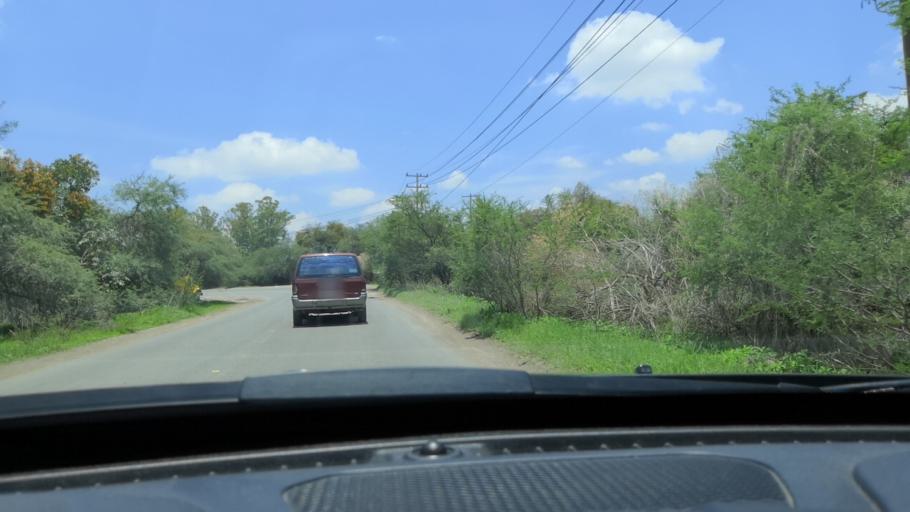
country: MX
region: Guanajuato
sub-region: Leon
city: Ladrilleras del Refugio
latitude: 21.0494
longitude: -101.5646
